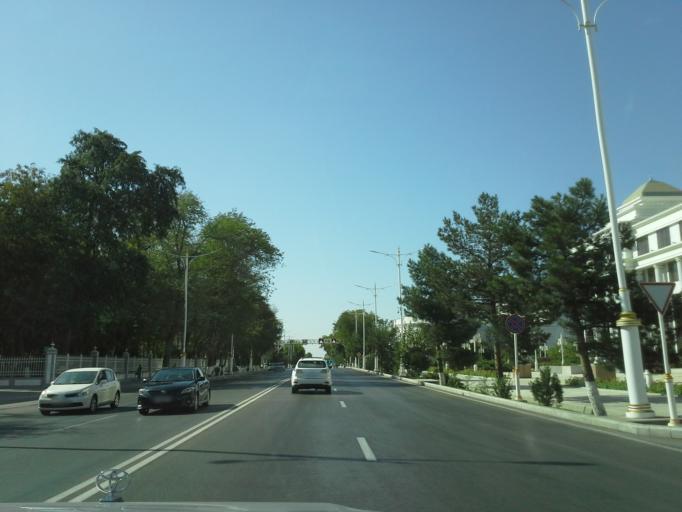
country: TM
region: Ahal
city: Ashgabat
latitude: 37.9400
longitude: 58.3921
